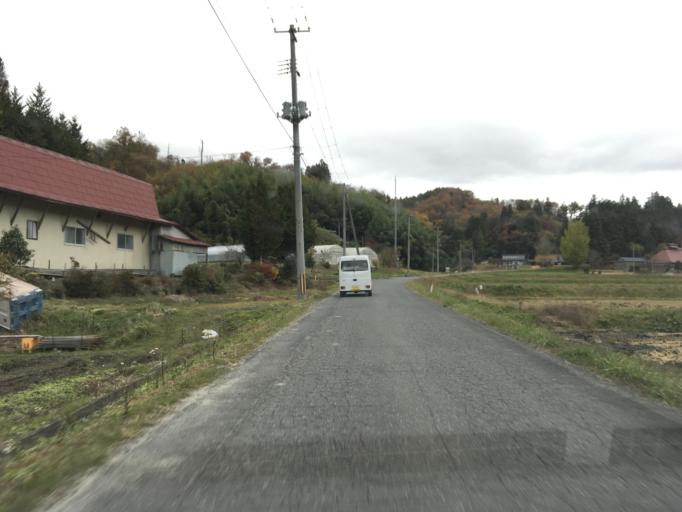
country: JP
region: Iwate
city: Mizusawa
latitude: 39.0461
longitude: 141.3319
